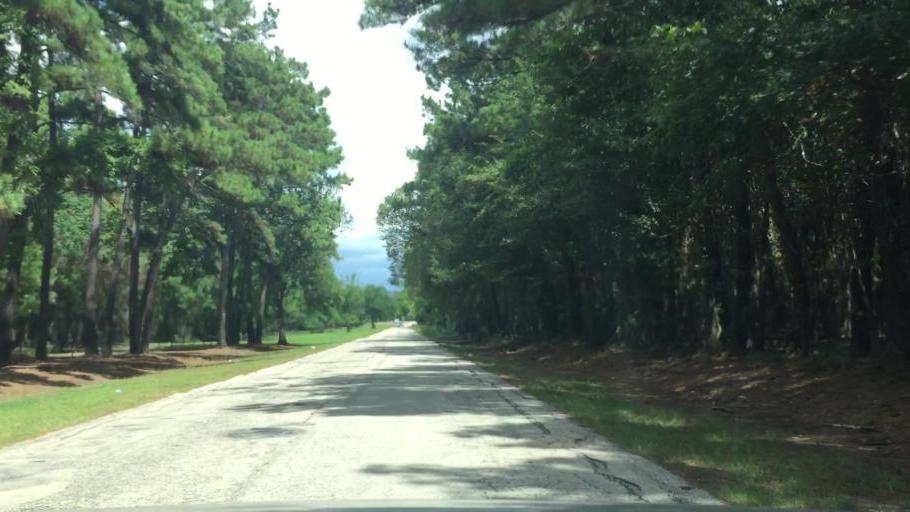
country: US
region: Texas
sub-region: Harris County
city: Jersey Village
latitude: 29.8132
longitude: -95.6223
